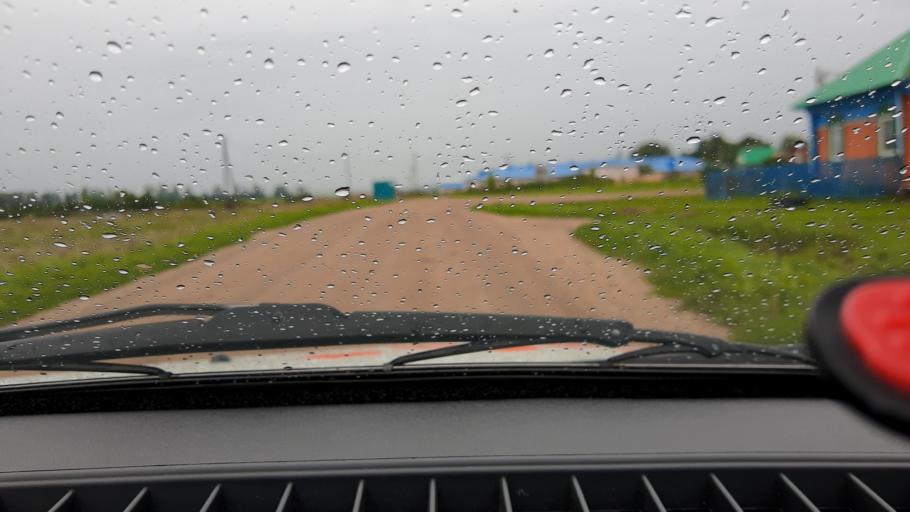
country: RU
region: Bashkortostan
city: Karmaskaly
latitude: 54.3815
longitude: 56.1140
